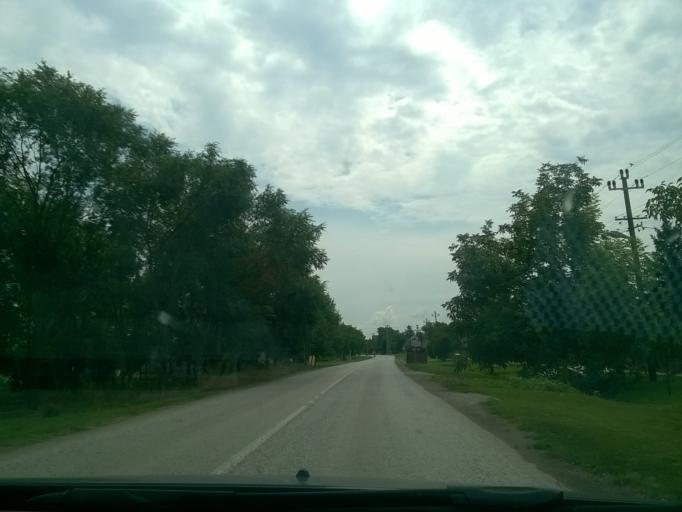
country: RS
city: Konak
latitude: 45.3168
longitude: 20.9074
